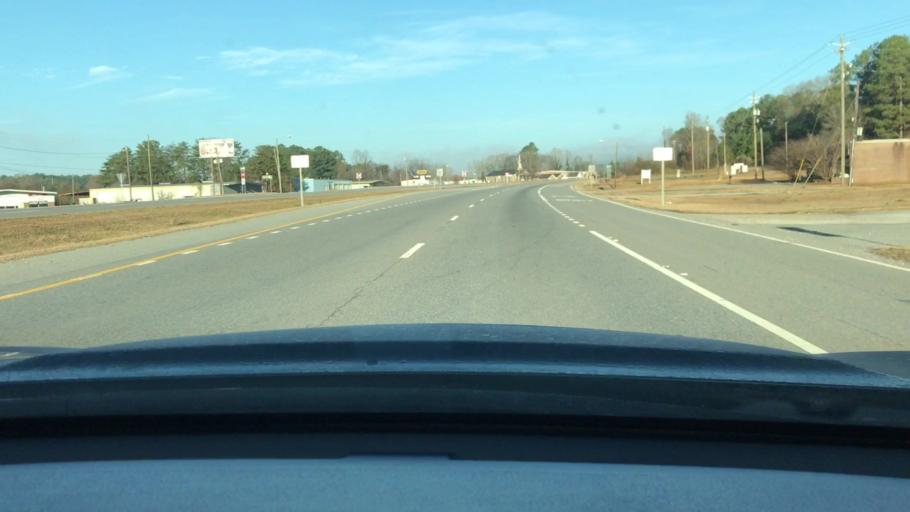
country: US
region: Alabama
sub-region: Talladega County
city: Mignon
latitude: 33.1793
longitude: -86.2970
